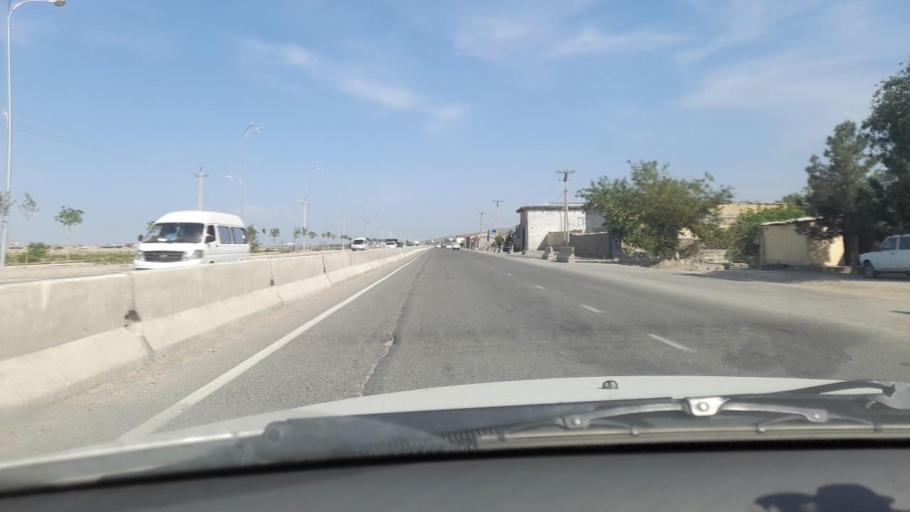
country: UZ
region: Samarqand
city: Samarqand
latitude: 39.7055
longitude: 66.9966
